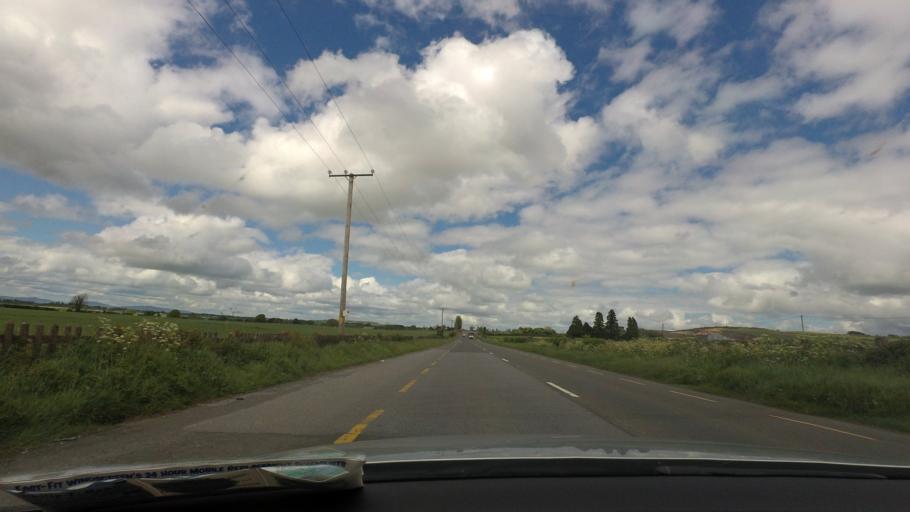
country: IE
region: Munster
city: Cashel
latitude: 52.5395
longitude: -7.8712
